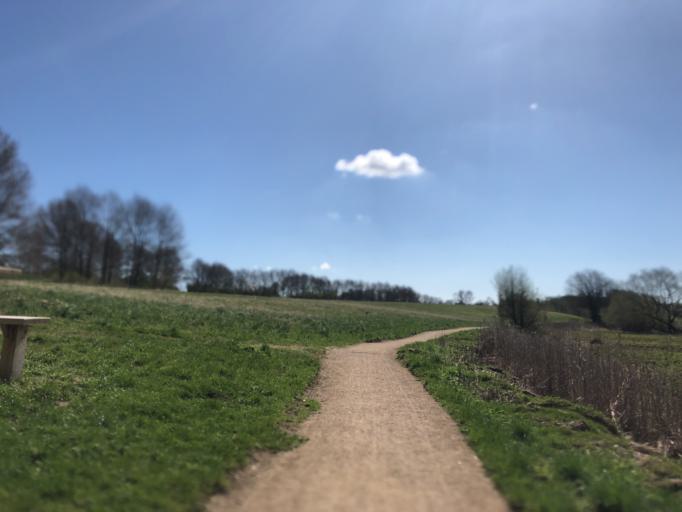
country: DK
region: Zealand
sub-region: Ringsted Kommune
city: Ringsted
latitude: 55.4248
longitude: 11.7752
